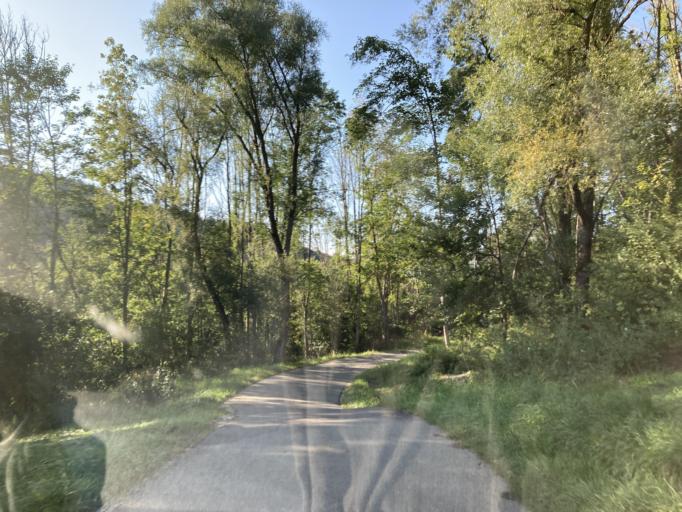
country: DE
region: Baden-Wuerttemberg
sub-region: Freiburg Region
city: Blumberg
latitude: 47.8245
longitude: 8.5101
